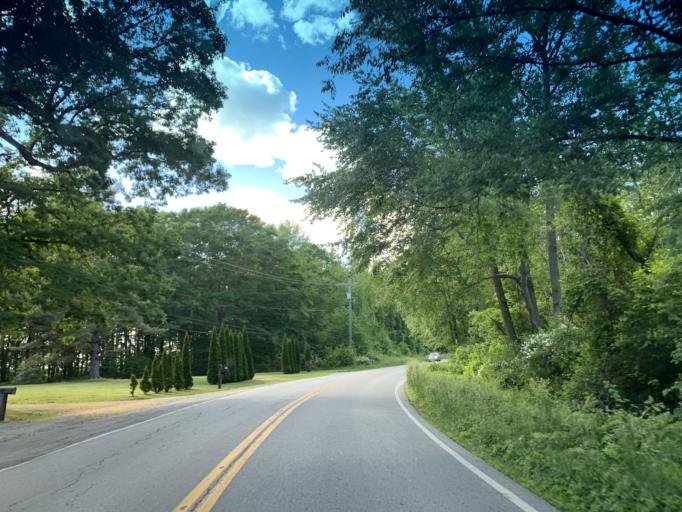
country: US
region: Maryland
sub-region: Cecil County
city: North East
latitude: 39.5755
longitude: -75.9419
